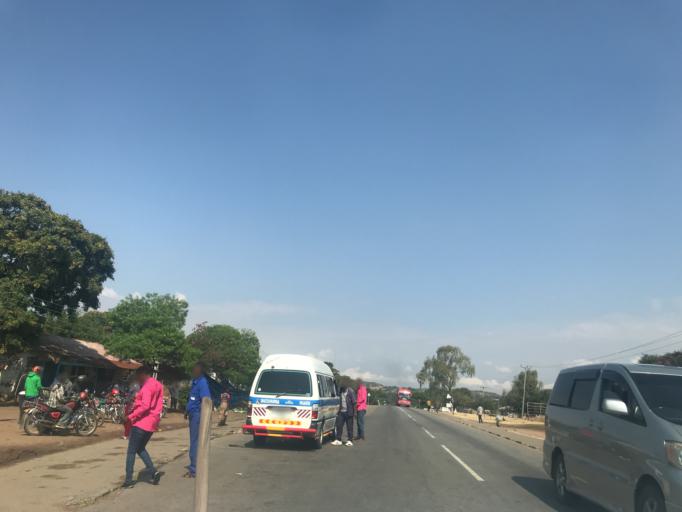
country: TZ
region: Mwanza
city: Nyanguge
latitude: -2.5392
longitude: 33.1979
